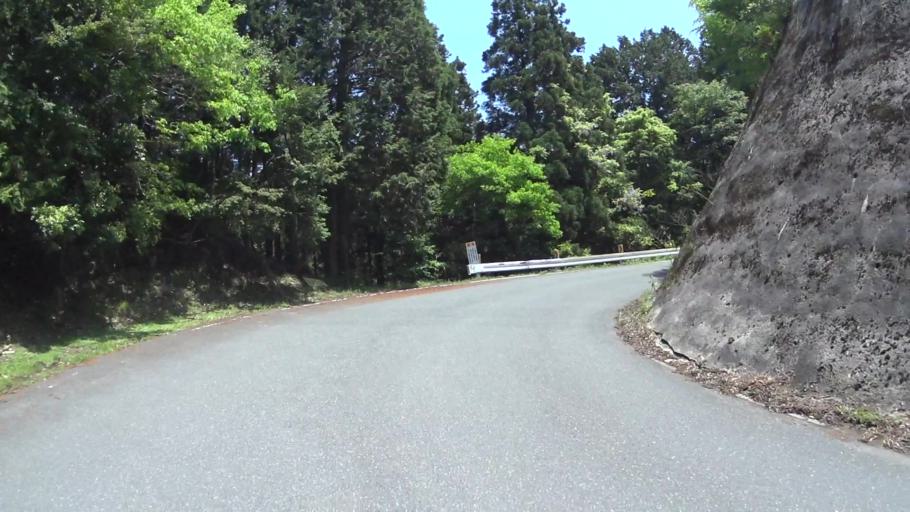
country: JP
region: Kyoto
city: Kameoka
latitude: 35.1234
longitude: 135.5873
